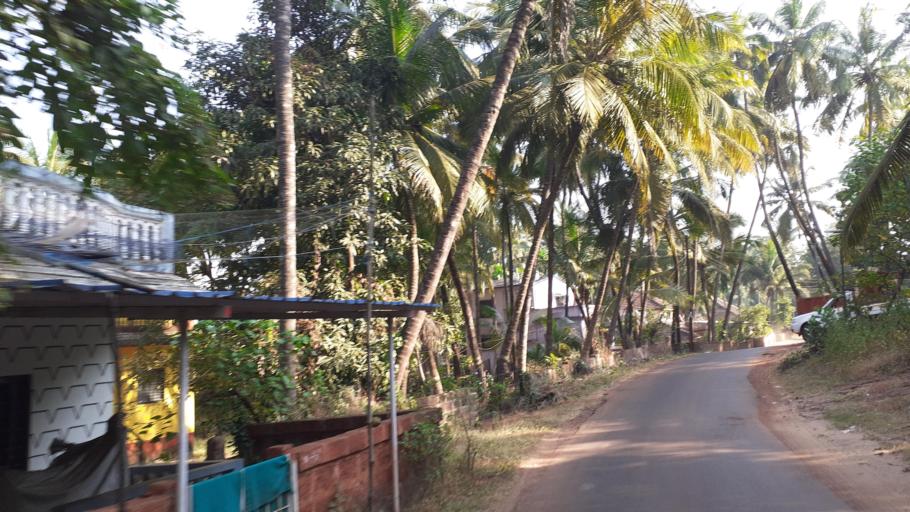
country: IN
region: Maharashtra
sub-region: Ratnagiri
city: Ratnagiri
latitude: 17.2171
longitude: 73.2475
